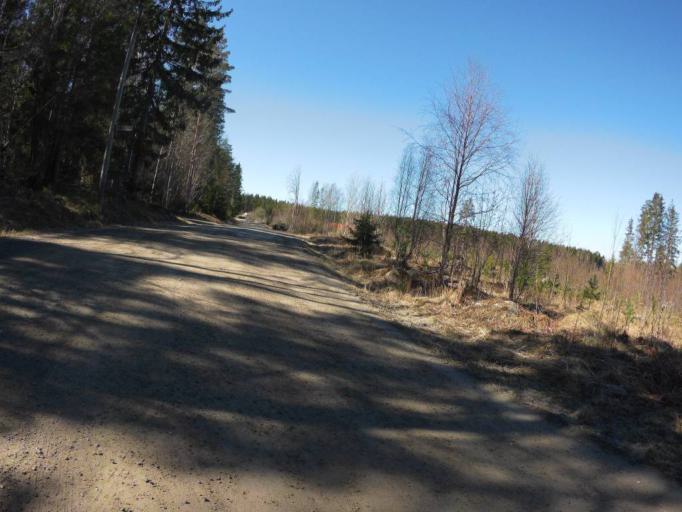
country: SE
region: Gaevleborg
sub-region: Gavle Kommun
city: Gavle
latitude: 60.7320
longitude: 17.2069
